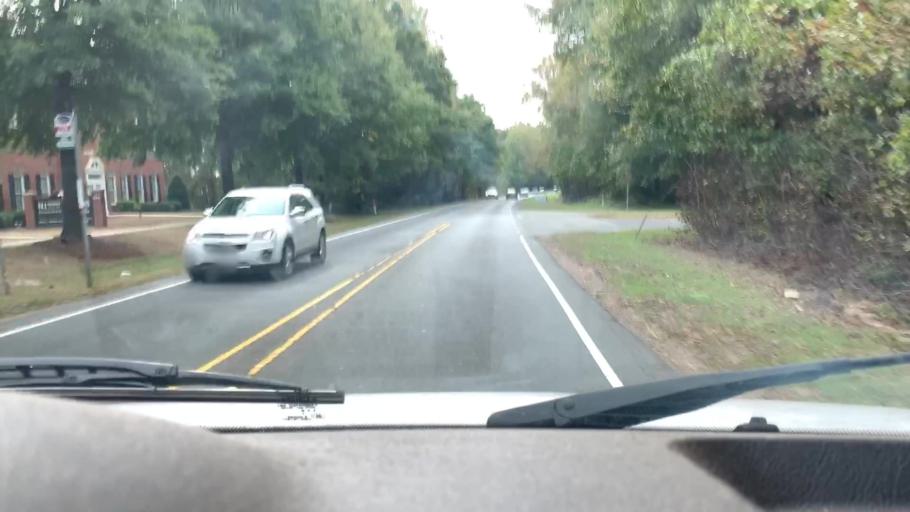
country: US
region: North Carolina
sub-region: Mecklenburg County
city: Cornelius
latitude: 35.4570
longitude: -80.8682
